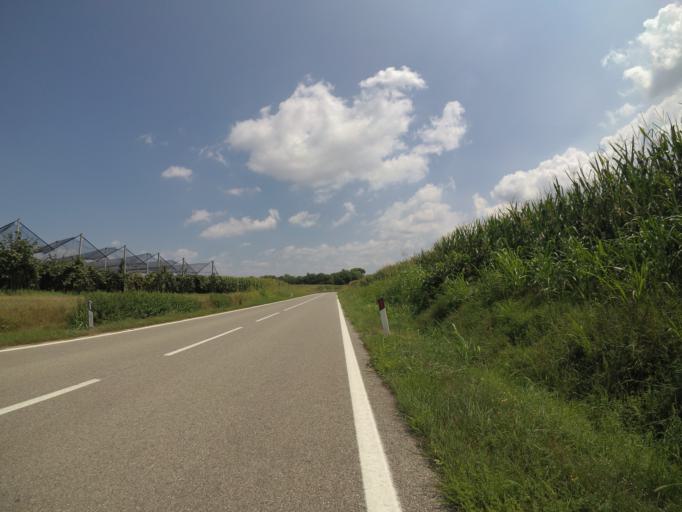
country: IT
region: Friuli Venezia Giulia
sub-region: Provincia di Udine
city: Sedegliano
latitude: 46.0186
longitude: 12.9998
